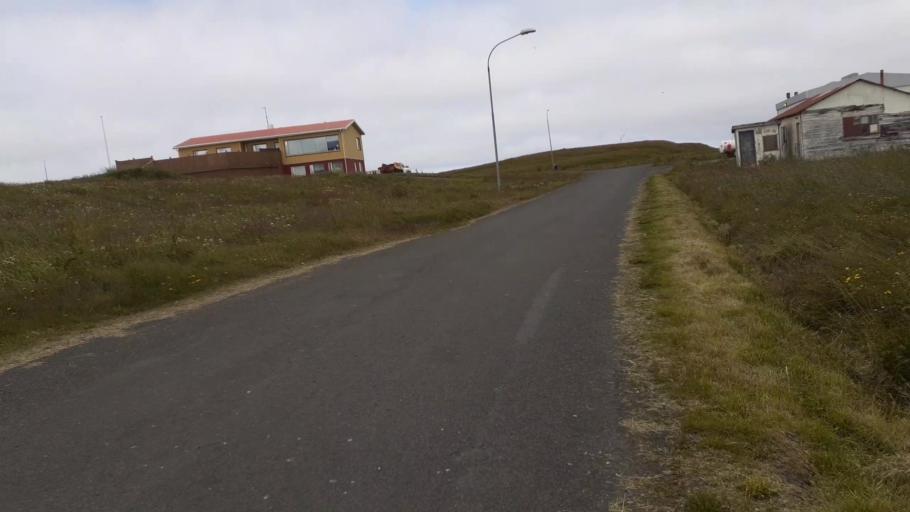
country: IS
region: Northeast
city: Dalvik
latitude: 66.5397
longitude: -18.0162
